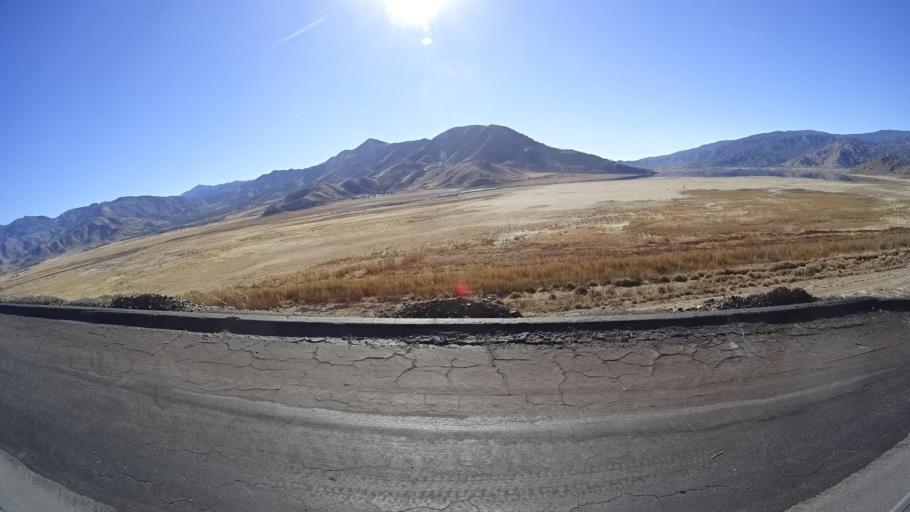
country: US
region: California
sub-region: Kern County
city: Wofford Heights
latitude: 35.6771
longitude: -118.4159
